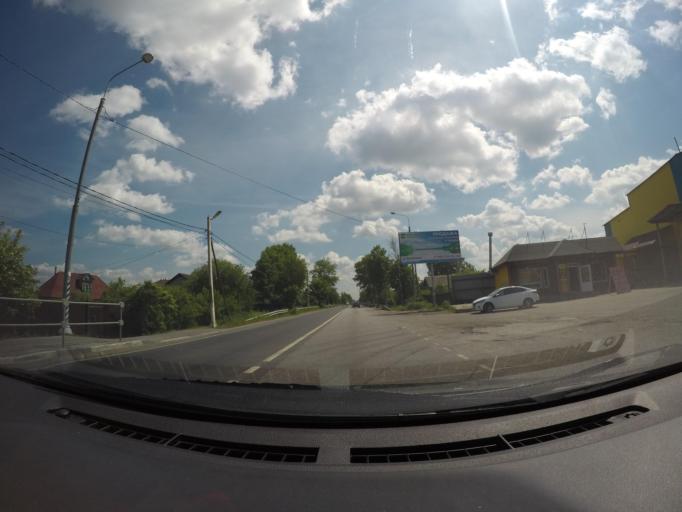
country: RU
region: Moskovskaya
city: Gzhel'
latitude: 55.6274
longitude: 38.3672
